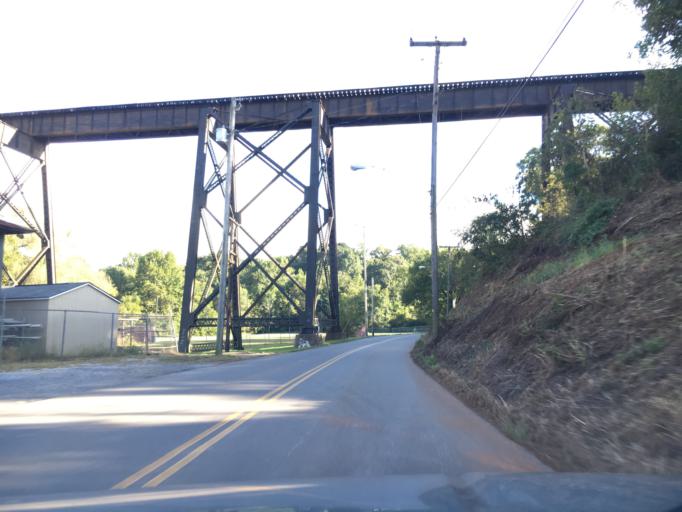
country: US
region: Virginia
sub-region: City of Lynchburg
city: West Lynchburg
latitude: 37.3934
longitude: -79.1568
